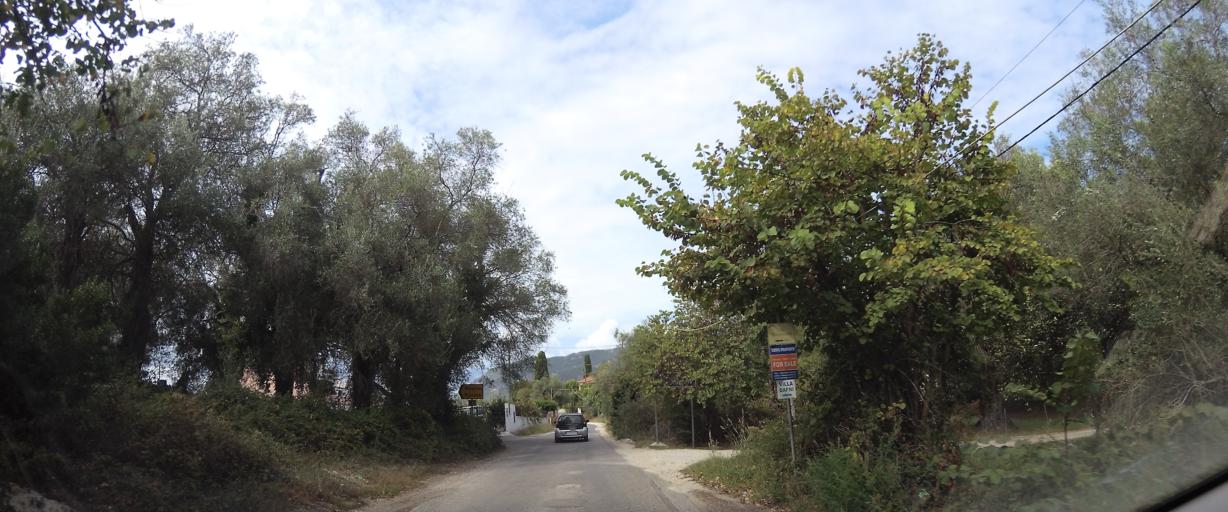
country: GR
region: Ionian Islands
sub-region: Nomos Kerkyras
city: Kontokali
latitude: 39.6929
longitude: 19.8121
